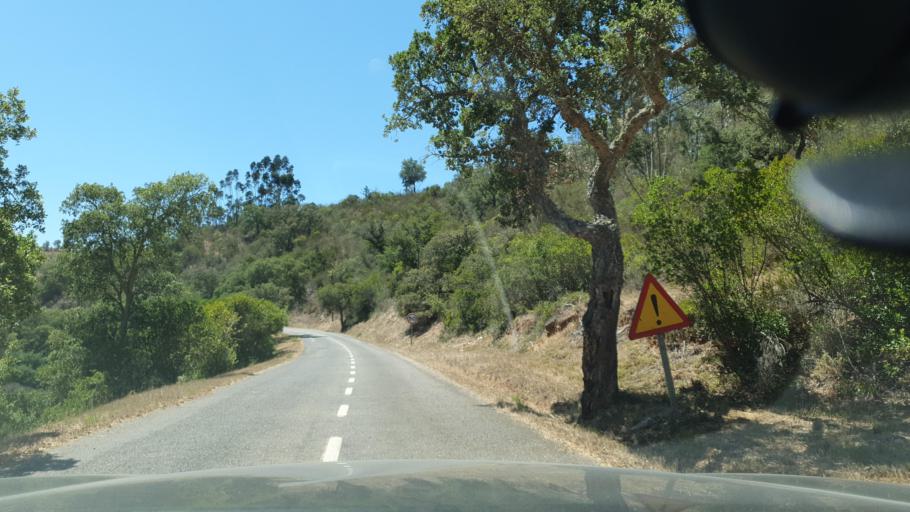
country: PT
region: Beja
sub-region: Odemira
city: Odemira
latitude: 37.6023
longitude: -8.5880
